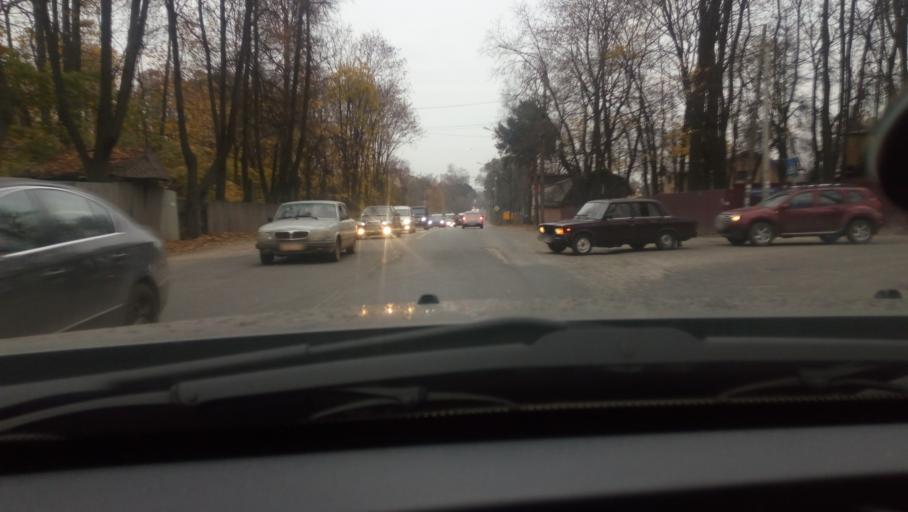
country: RU
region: Moskovskaya
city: Saltykovka
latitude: 55.7512
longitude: 37.9255
